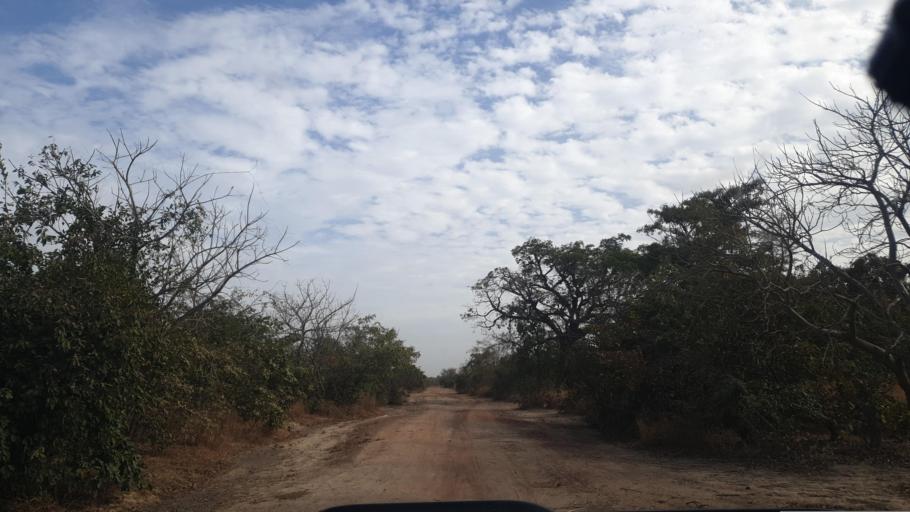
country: ML
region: Sikasso
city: Yanfolila
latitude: 11.4093
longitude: -8.0082
